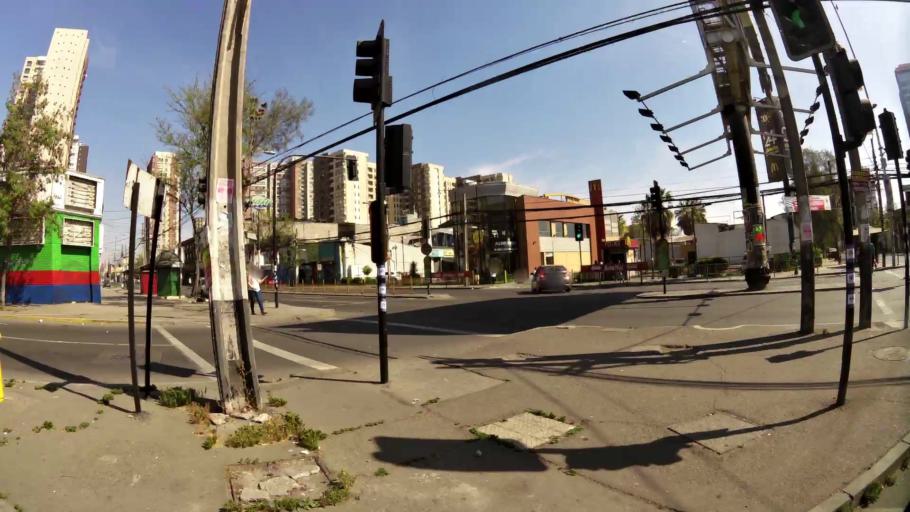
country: CL
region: Santiago Metropolitan
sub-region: Provincia de Santiago
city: Santiago
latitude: -33.4207
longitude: -70.6557
